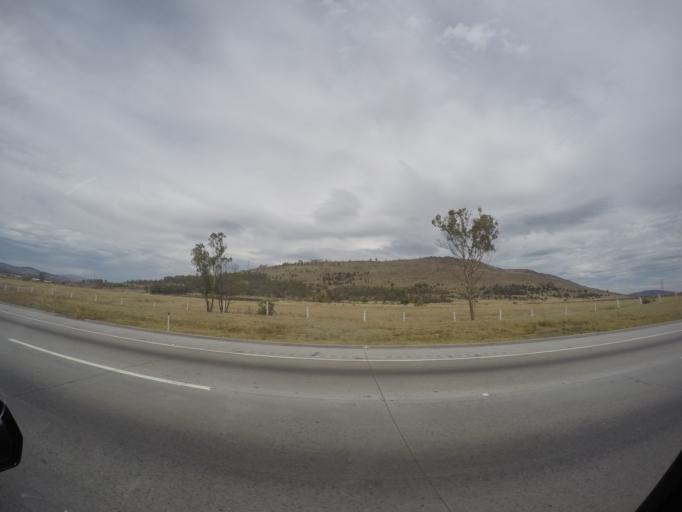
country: MX
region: Mexico
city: San Francisco Soyaniquilpan
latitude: 20.0062
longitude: -99.5027
